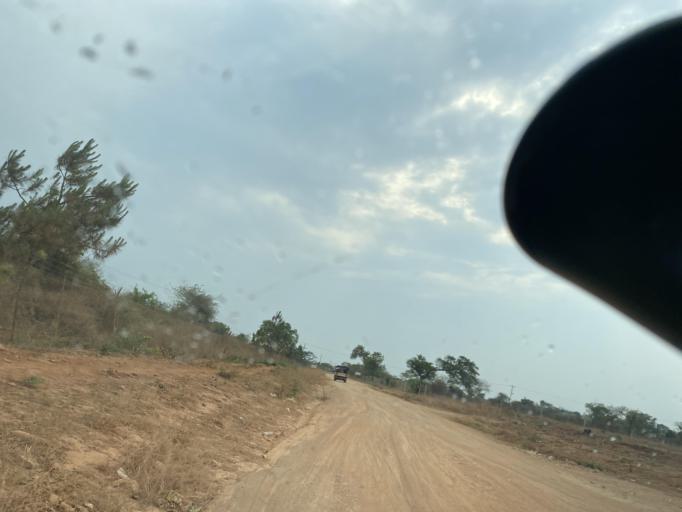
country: ZM
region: Lusaka
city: Lusaka
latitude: -15.2876
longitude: 28.2900
